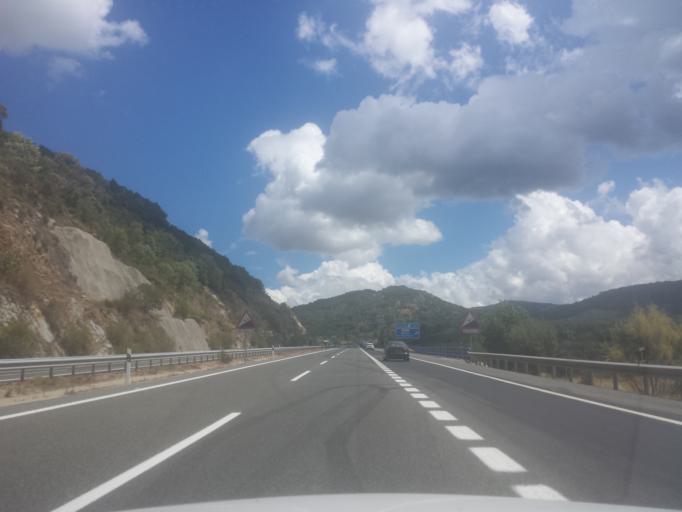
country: ES
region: Extremadura
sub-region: Provincia de Caceres
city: Banos de Montemayor
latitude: 40.3186
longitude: -5.8718
